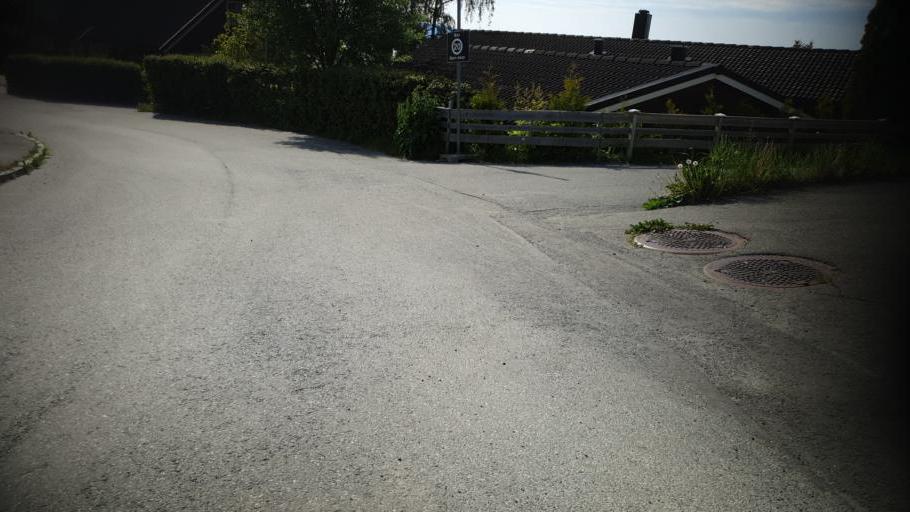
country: NO
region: Sor-Trondelag
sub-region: Malvik
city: Malvik
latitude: 63.4345
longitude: 10.5845
